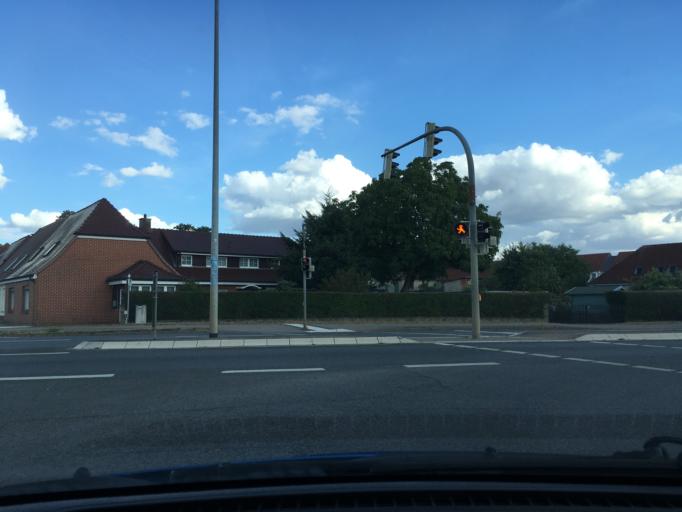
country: DE
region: Mecklenburg-Vorpommern
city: Ludwigslust
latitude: 53.3260
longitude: 11.5002
